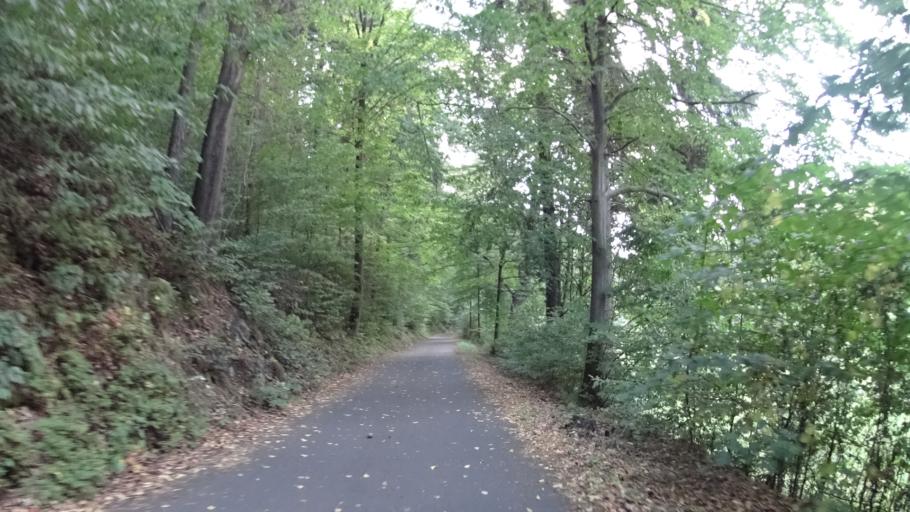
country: DE
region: Saxony
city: Ostritz
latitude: 50.9882
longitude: 14.9191
